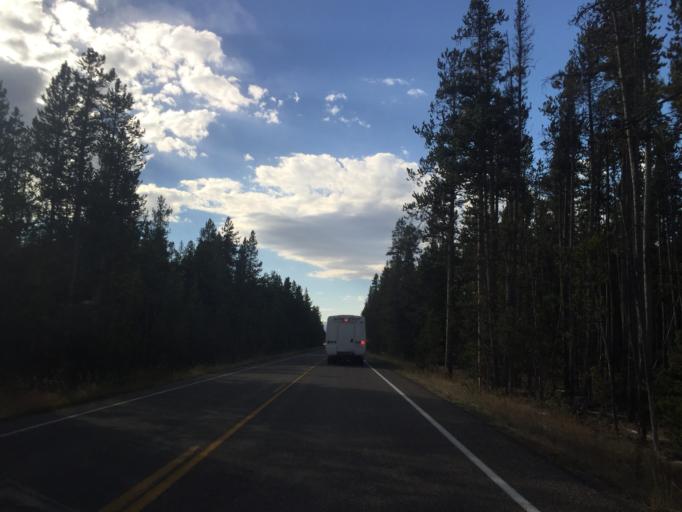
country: US
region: Montana
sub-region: Gallatin County
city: West Yellowstone
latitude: 44.6557
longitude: -111.0822
